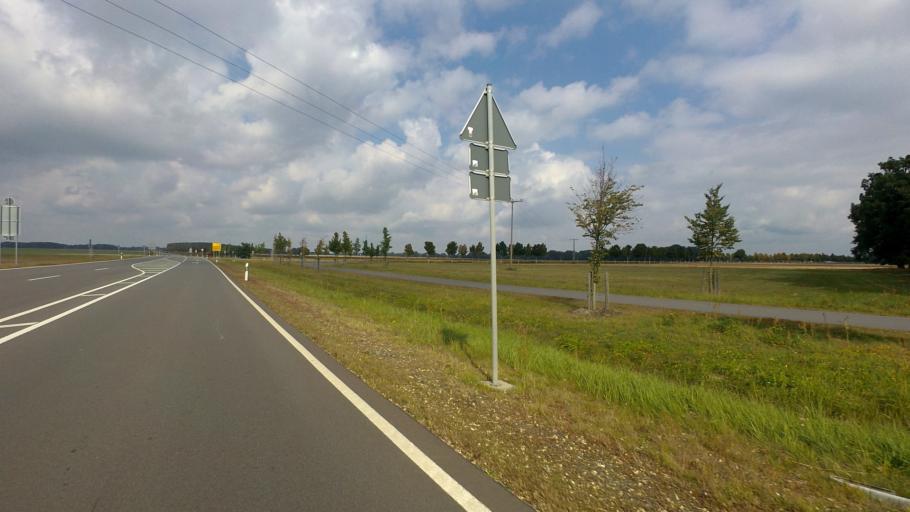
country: DE
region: Brandenburg
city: Herzberg
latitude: 51.6601
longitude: 13.2837
